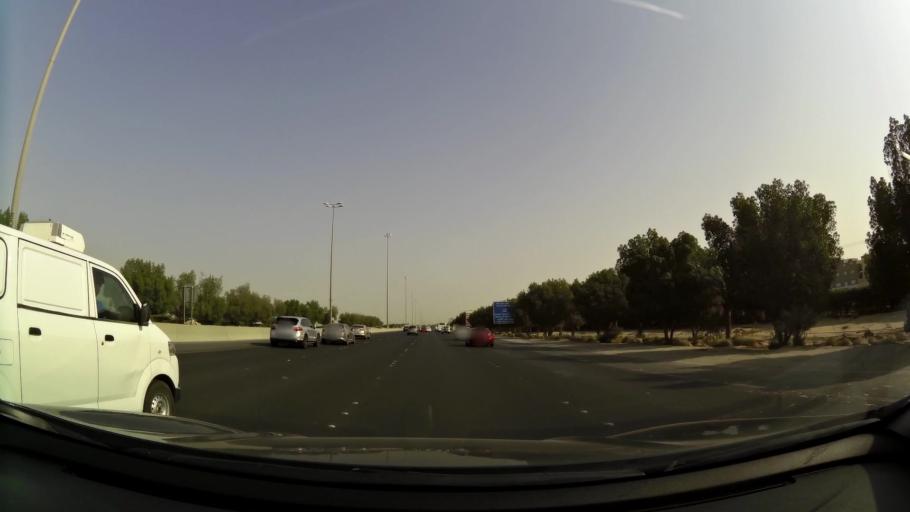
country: KW
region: Muhafazat al Jahra'
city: Al Jahra'
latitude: 29.3274
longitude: 47.7421
